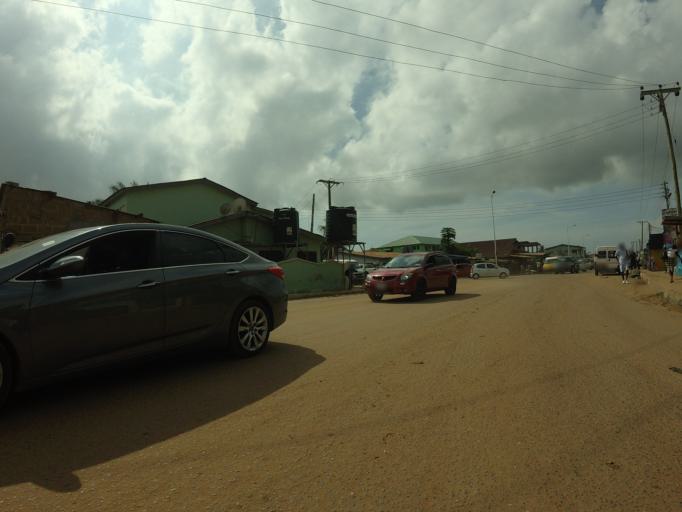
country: GH
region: Greater Accra
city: Teshi Old Town
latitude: 5.5961
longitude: -0.1310
